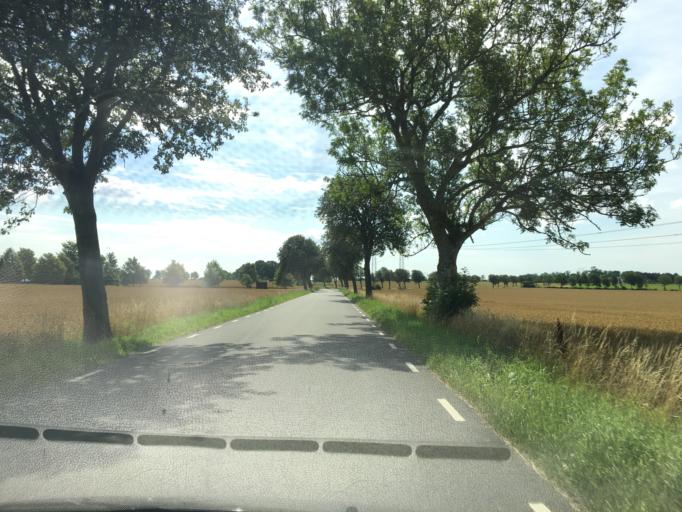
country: SE
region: Skane
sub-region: Svalovs Kommun
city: Svaloev
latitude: 55.9481
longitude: 13.0304
